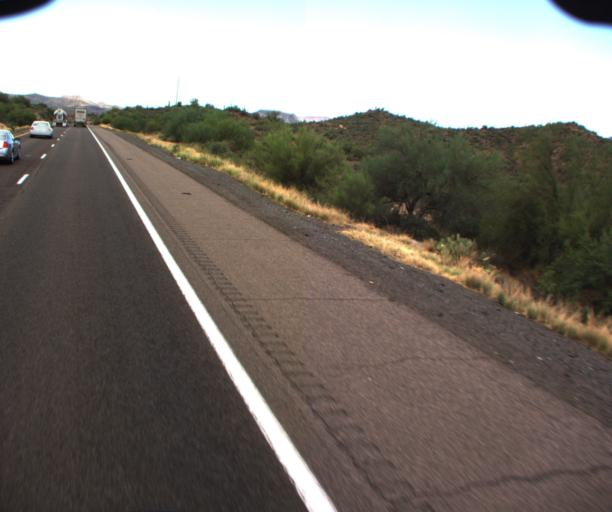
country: US
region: Arizona
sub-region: Yavapai County
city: Black Canyon City
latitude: 34.0269
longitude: -112.1472
